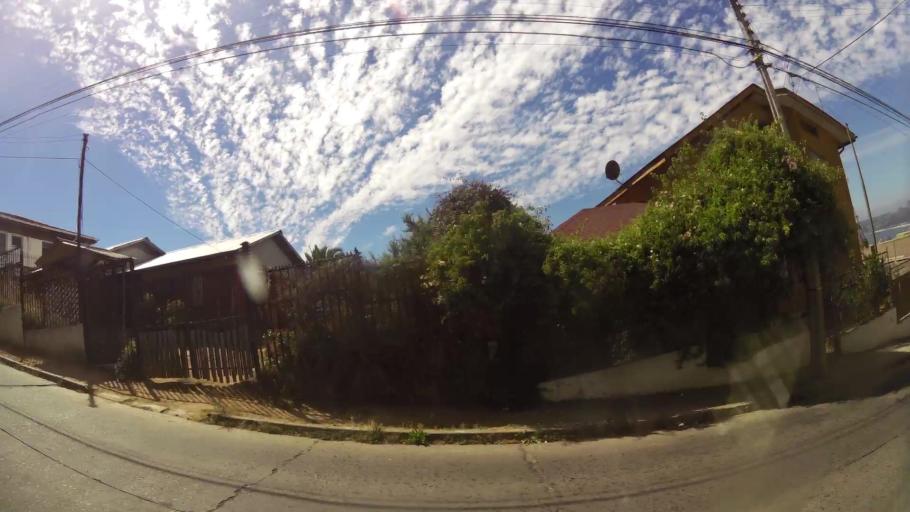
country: CL
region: Valparaiso
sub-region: Provincia de Valparaiso
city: Vina del Mar
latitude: -33.0366
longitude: -71.5801
